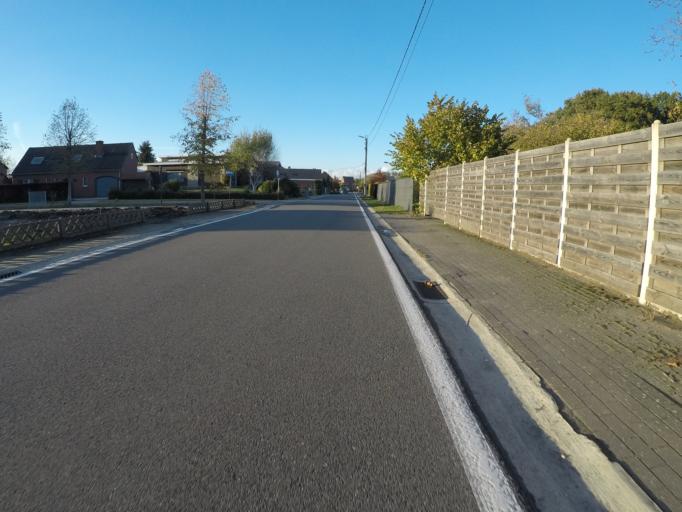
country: BE
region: Flanders
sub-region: Provincie Vlaams-Brabant
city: Begijnendijk
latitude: 51.0201
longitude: 4.8009
